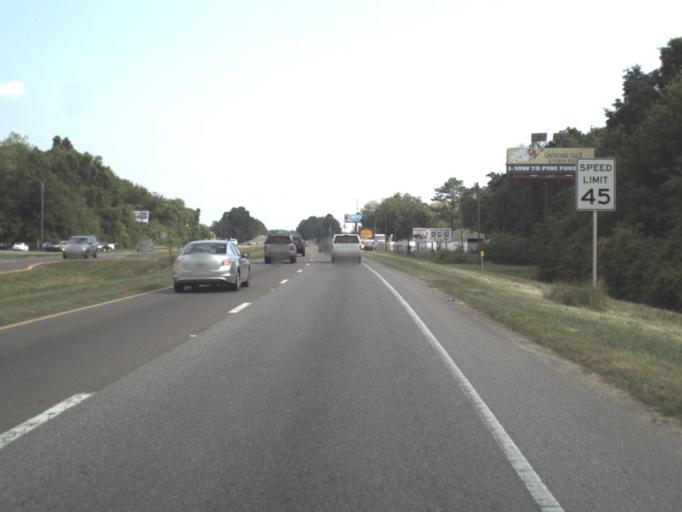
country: US
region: Florida
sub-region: Escambia County
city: Ensley
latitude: 30.5401
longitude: -87.2806
